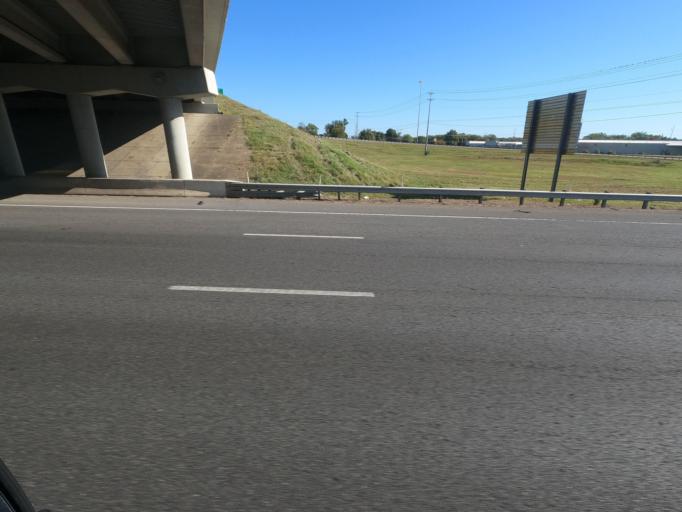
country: US
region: Tennessee
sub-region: Rutherford County
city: Murfreesboro
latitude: 35.8282
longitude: -86.4141
